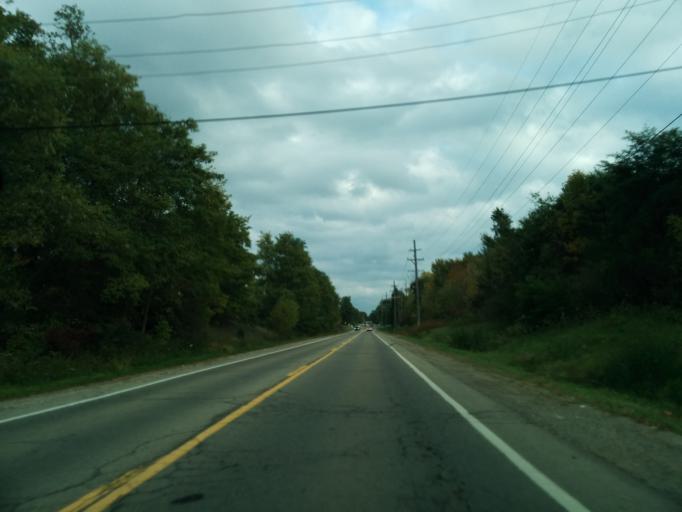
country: US
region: Michigan
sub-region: Oakland County
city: Waterford
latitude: 42.6932
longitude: -83.4947
